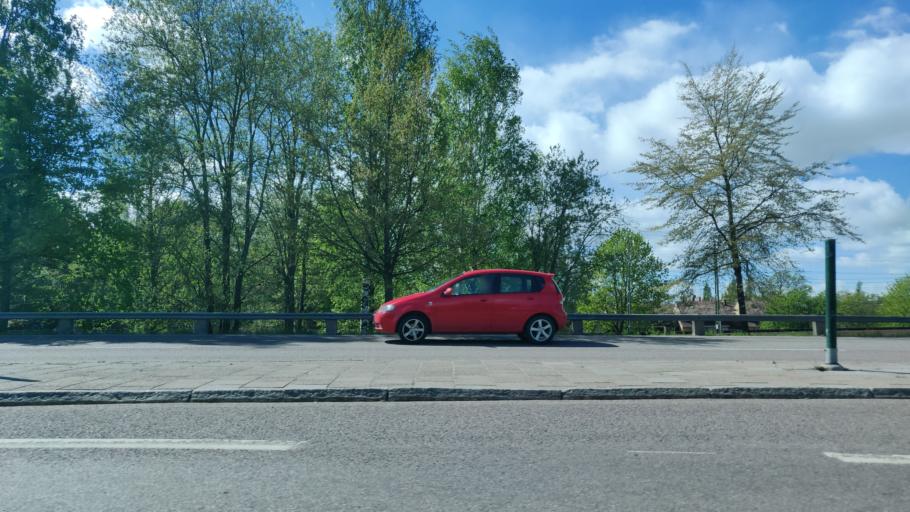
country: SE
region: Vaermland
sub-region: Karlstads Kommun
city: Karlstad
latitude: 59.3793
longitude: 13.4890
